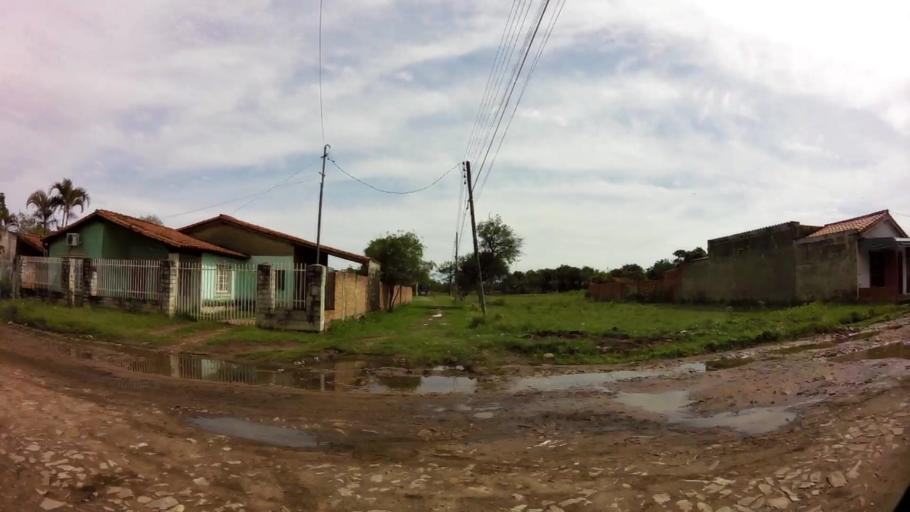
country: PY
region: Central
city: Limpio
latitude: -25.1664
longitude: -57.4826
